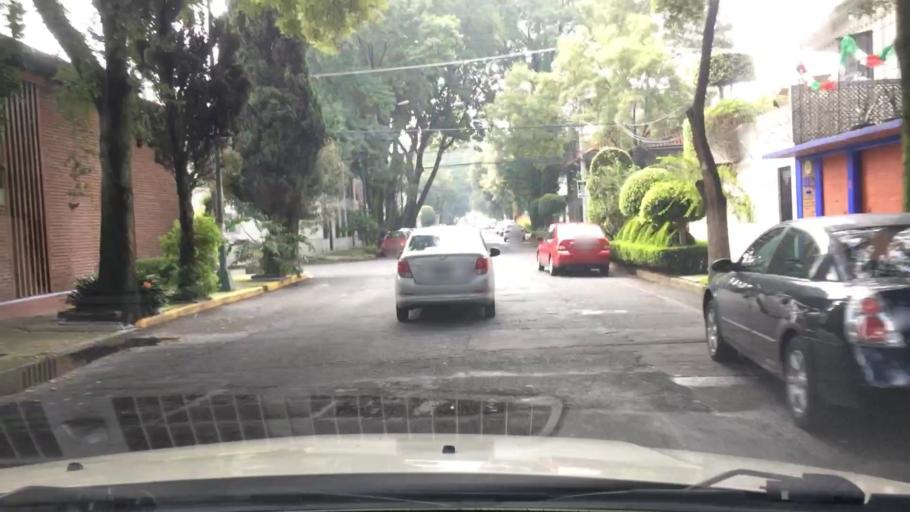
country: MX
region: Mexico City
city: Coyoacan
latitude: 19.3553
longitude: -99.1576
